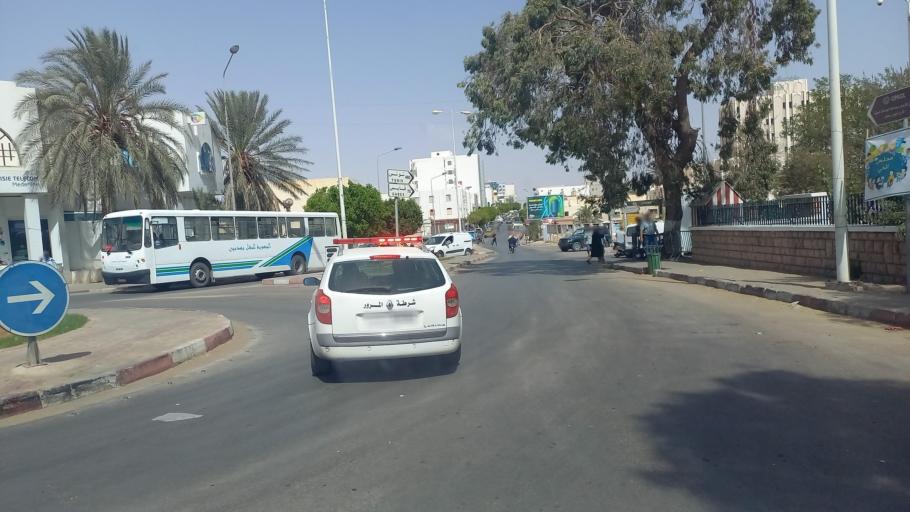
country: TN
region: Madanin
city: Medenine
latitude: 33.3434
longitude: 10.4912
